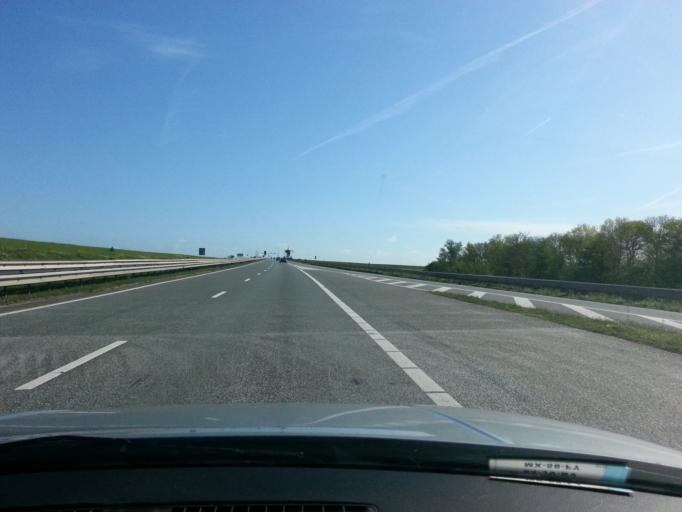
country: NL
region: Flevoland
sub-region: Gemeente Urk
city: Urk
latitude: 52.6068
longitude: 5.6349
